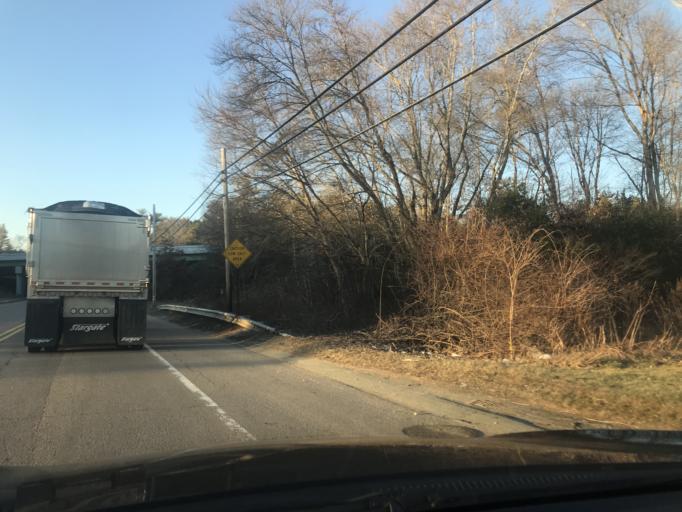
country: US
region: Massachusetts
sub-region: Plymouth County
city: Middleborough Center
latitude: 41.8454
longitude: -70.8489
